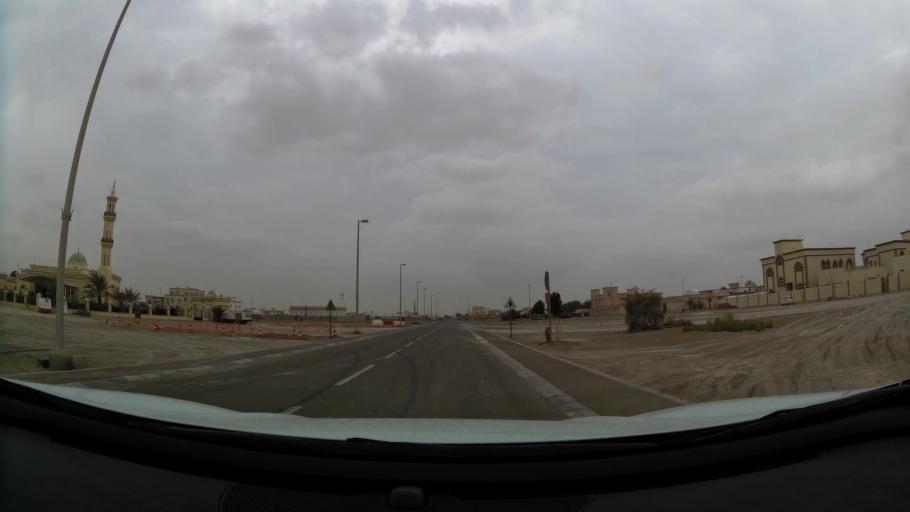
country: AE
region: Abu Dhabi
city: Abu Dhabi
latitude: 24.3580
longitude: 54.6616
